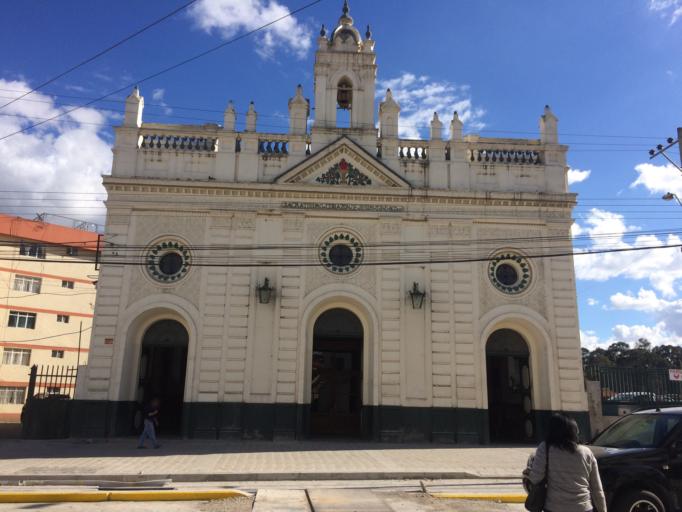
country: EC
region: Azuay
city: Cuenca
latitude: -2.8931
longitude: -79.0147
